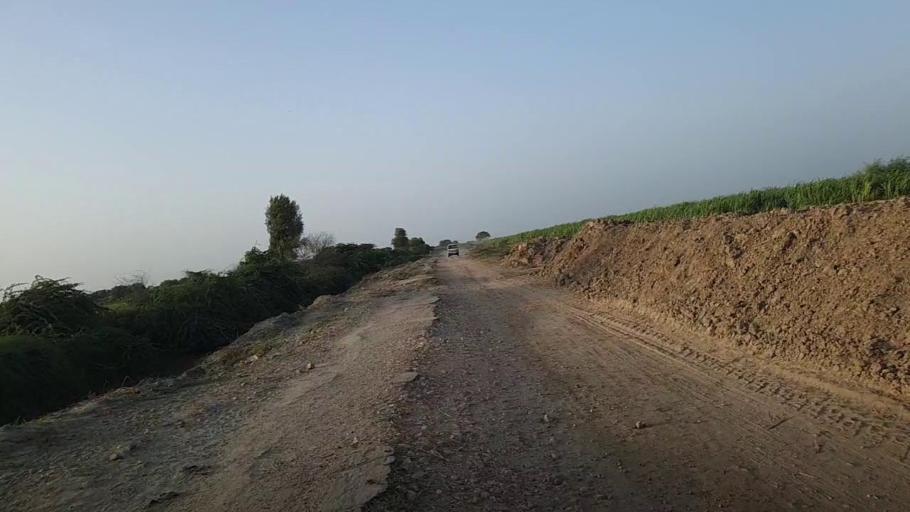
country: PK
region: Sindh
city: Kario
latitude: 24.7041
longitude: 68.4649
